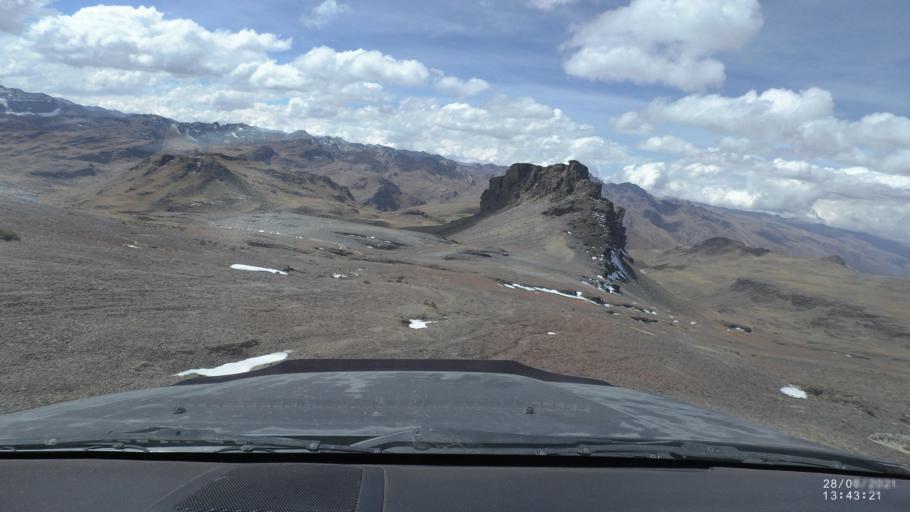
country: BO
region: Cochabamba
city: Sipe Sipe
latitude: -17.2833
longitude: -66.3838
